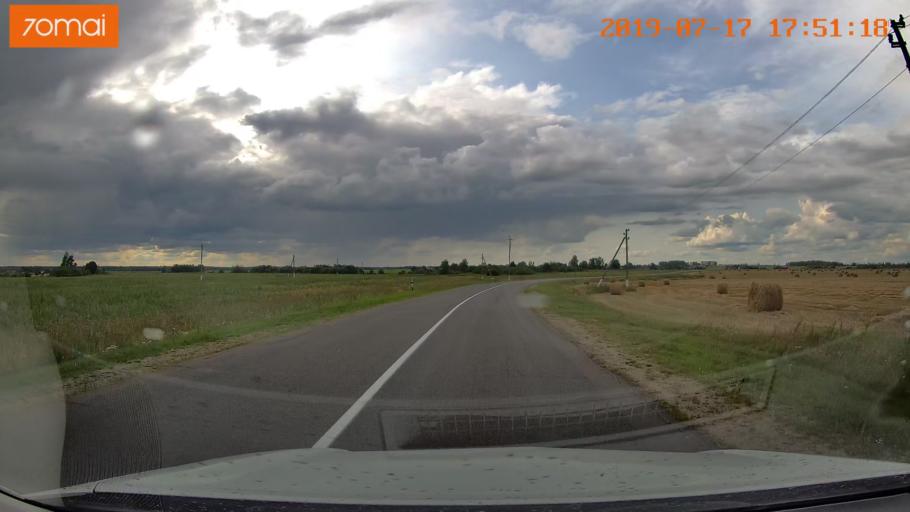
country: BY
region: Mogilev
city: Hlusha
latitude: 53.1503
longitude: 28.7895
